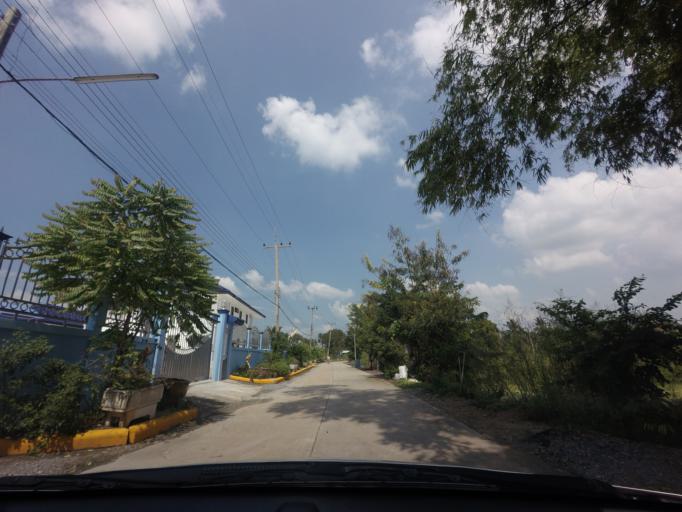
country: TH
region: Nakhon Pathom
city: Nakhon Chai Si
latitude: 13.8106
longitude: 100.1886
